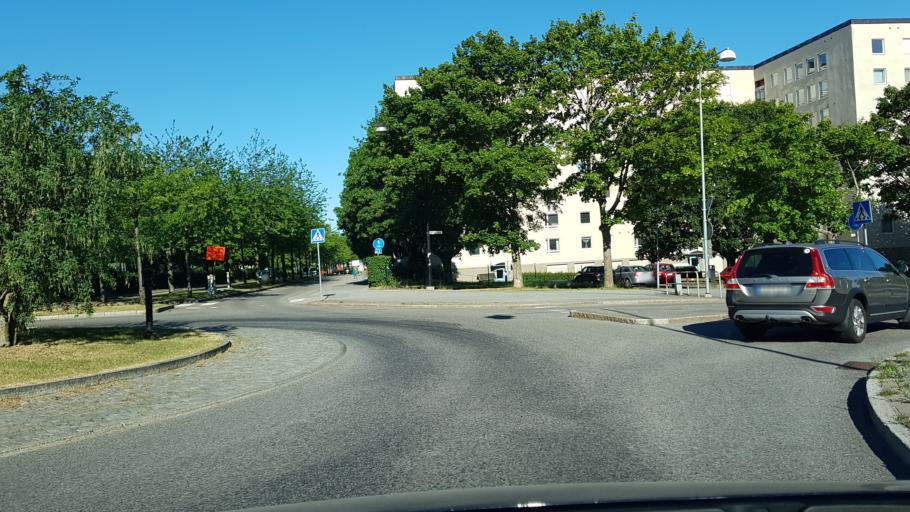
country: SE
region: Stockholm
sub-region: Jarfalla Kommun
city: Jakobsberg
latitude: 59.4214
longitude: 17.8451
